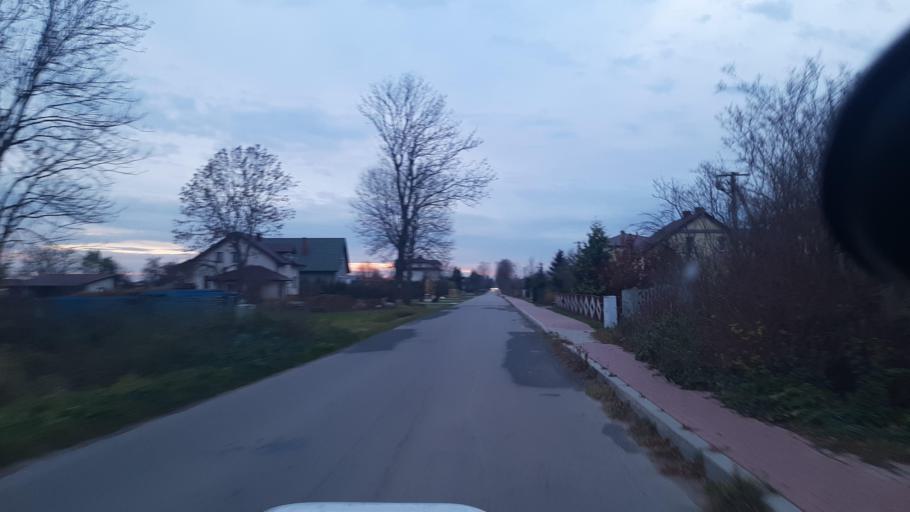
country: PL
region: Lublin Voivodeship
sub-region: Powiat lubelski
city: Garbow
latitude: 51.3653
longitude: 22.3835
